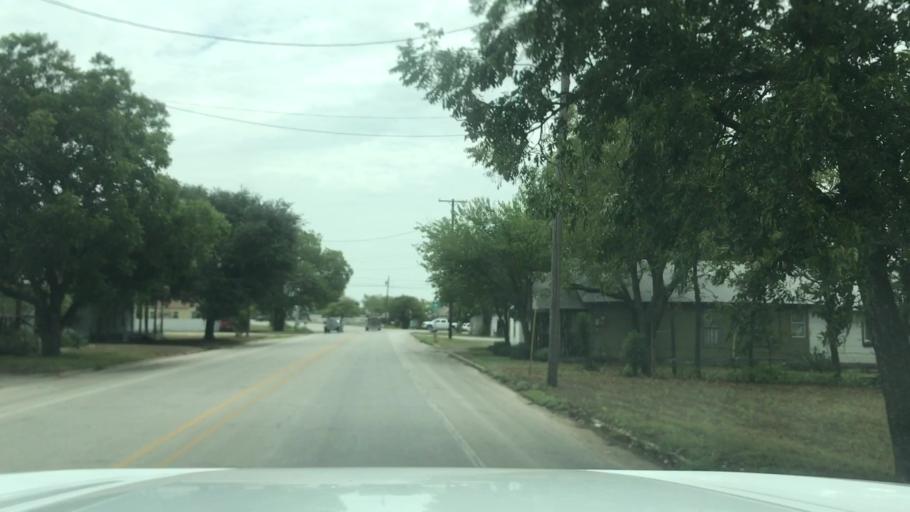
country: US
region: Texas
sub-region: Erath County
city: Dublin
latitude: 32.0835
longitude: -98.3358
